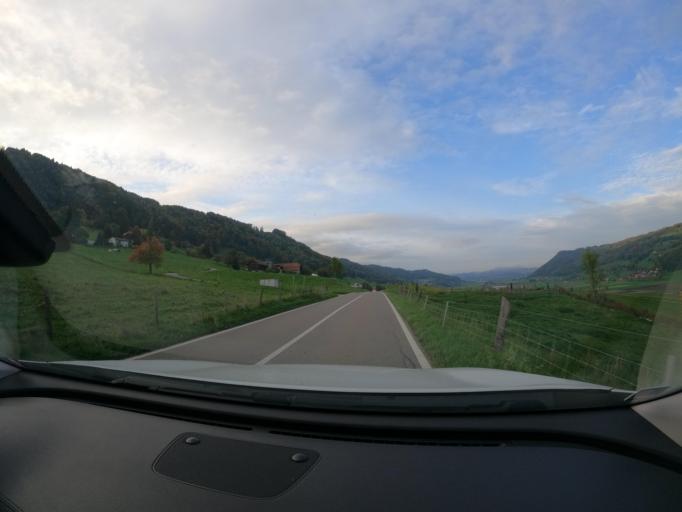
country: CH
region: Bern
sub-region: Bern-Mittelland District
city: Toffen
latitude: 46.8442
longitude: 7.4923
